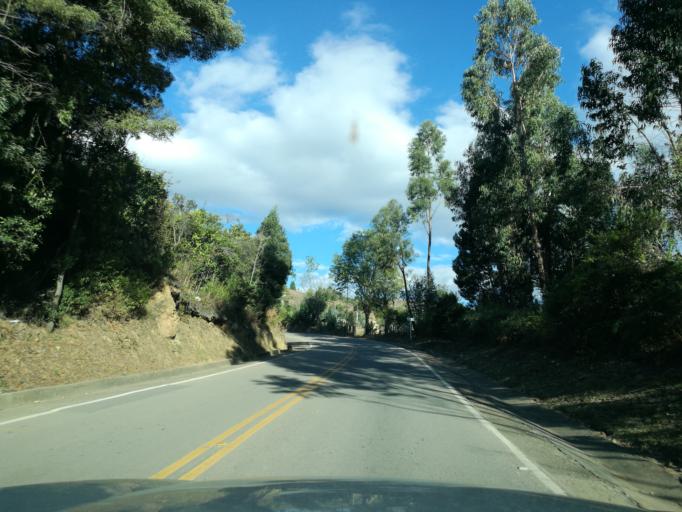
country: CO
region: Boyaca
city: Raquira
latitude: 5.5661
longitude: -73.6691
